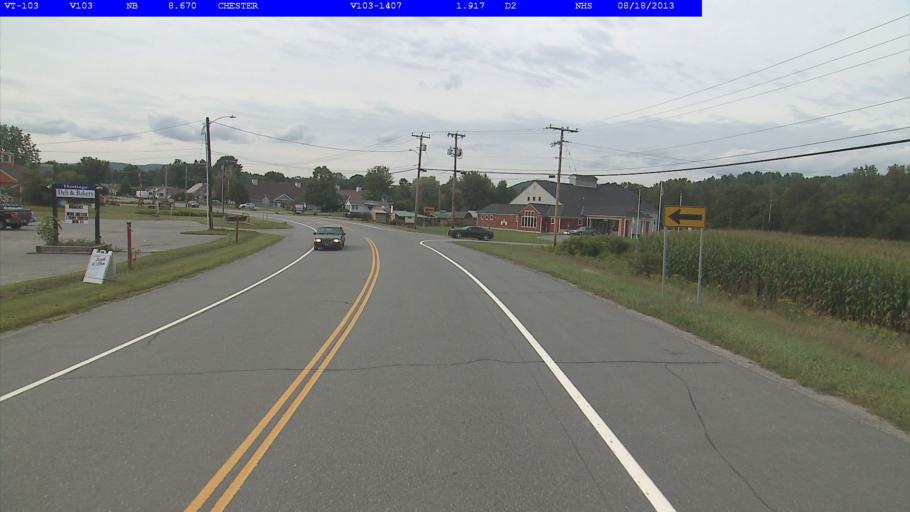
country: US
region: Vermont
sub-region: Windsor County
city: Chester
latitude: 43.2548
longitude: -72.5783
